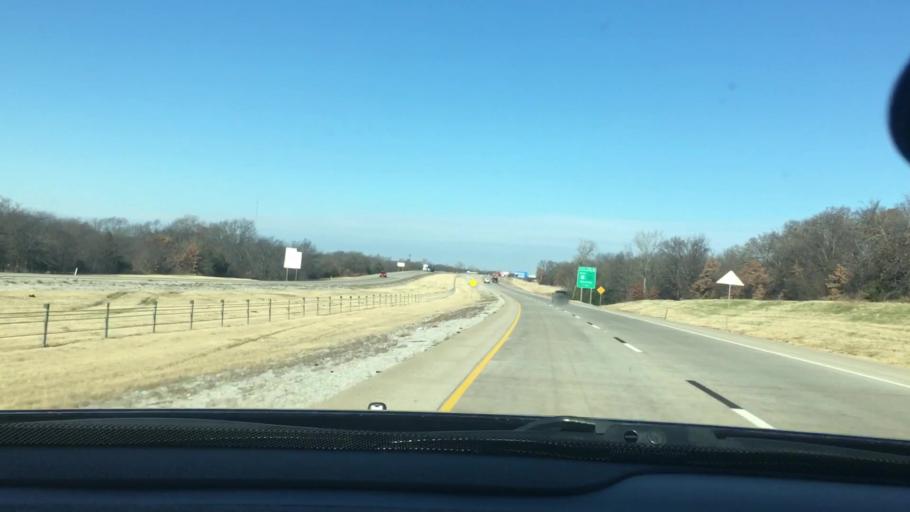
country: US
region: Oklahoma
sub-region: Carter County
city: Ardmore
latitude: 34.1539
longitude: -97.1593
